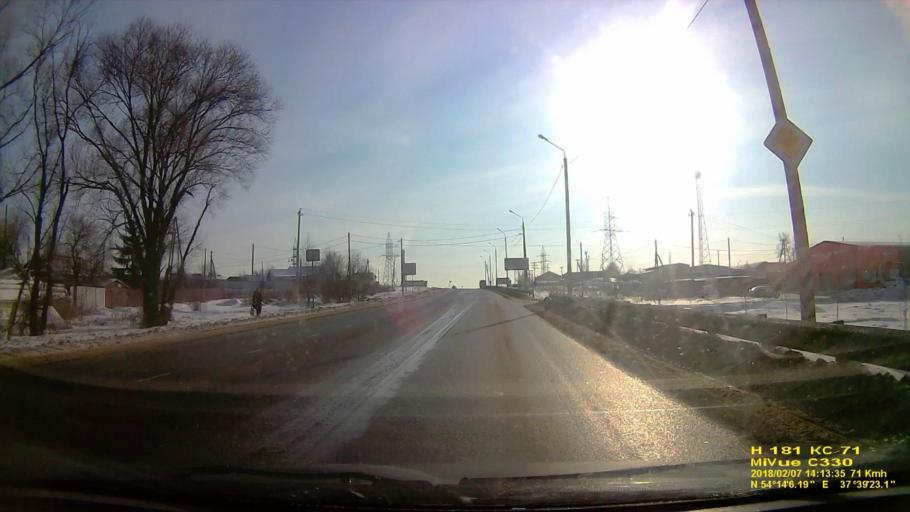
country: RU
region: Tula
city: Gorelki
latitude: 54.2349
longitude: 37.6564
